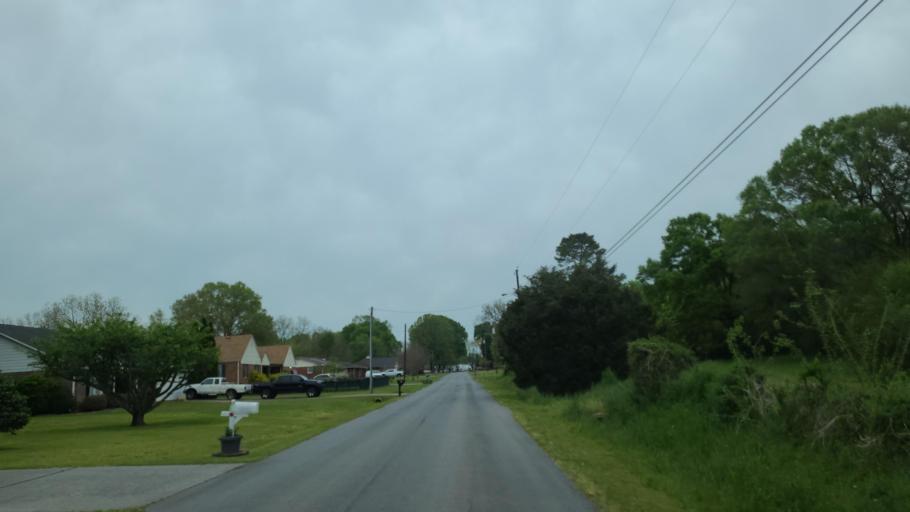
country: US
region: Georgia
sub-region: Bartow County
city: Cartersville
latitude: 34.2009
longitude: -84.8168
